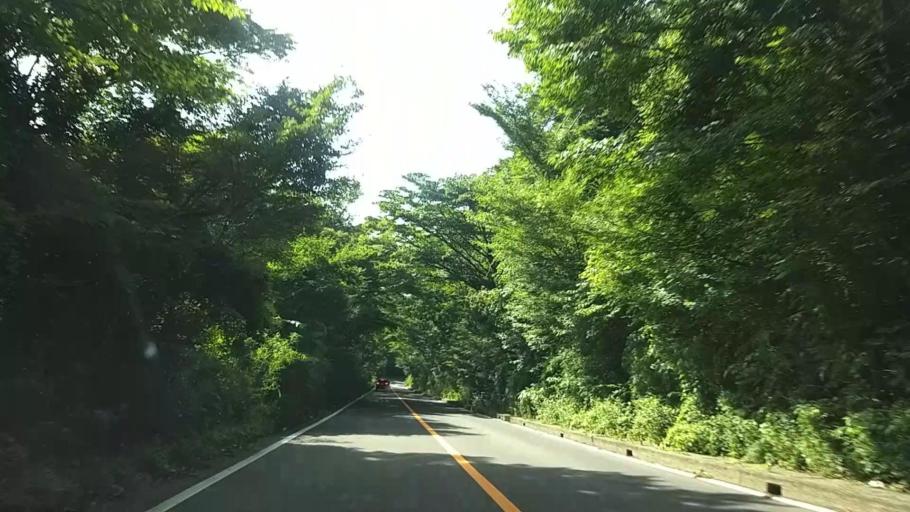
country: JP
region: Kanagawa
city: Hakone
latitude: 35.2234
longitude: 139.0062
